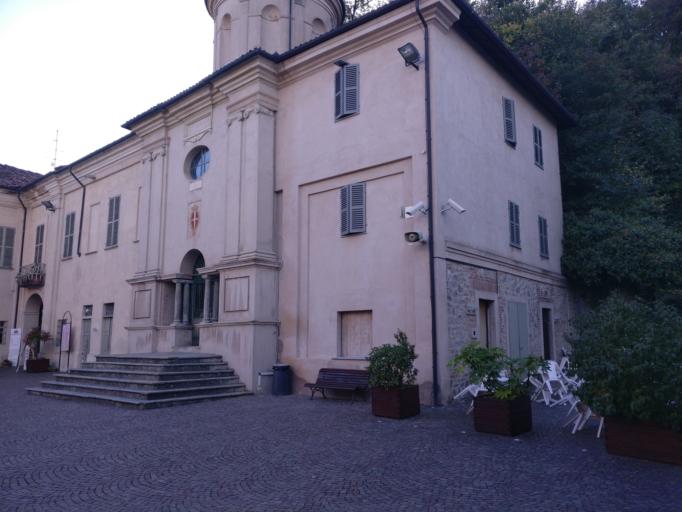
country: IT
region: Piedmont
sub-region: Provincia di Alessandria
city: Serralunga di Crea
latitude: 45.0944
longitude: 8.2757
